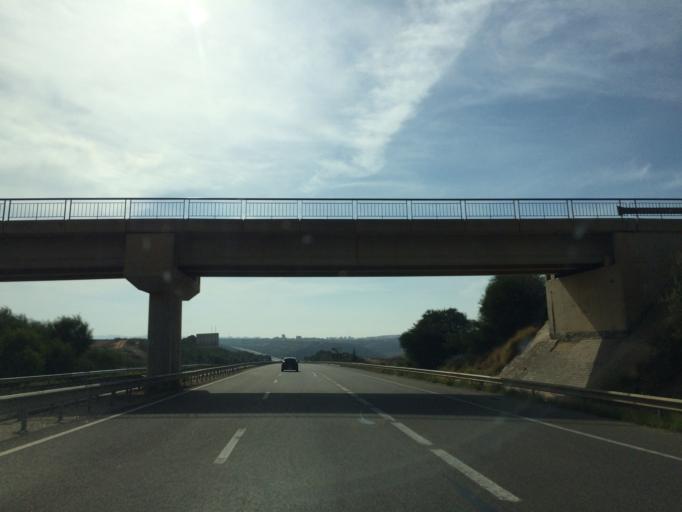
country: MA
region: Tanger-Tetouan
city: Asilah
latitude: 35.4671
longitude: -6.0066
